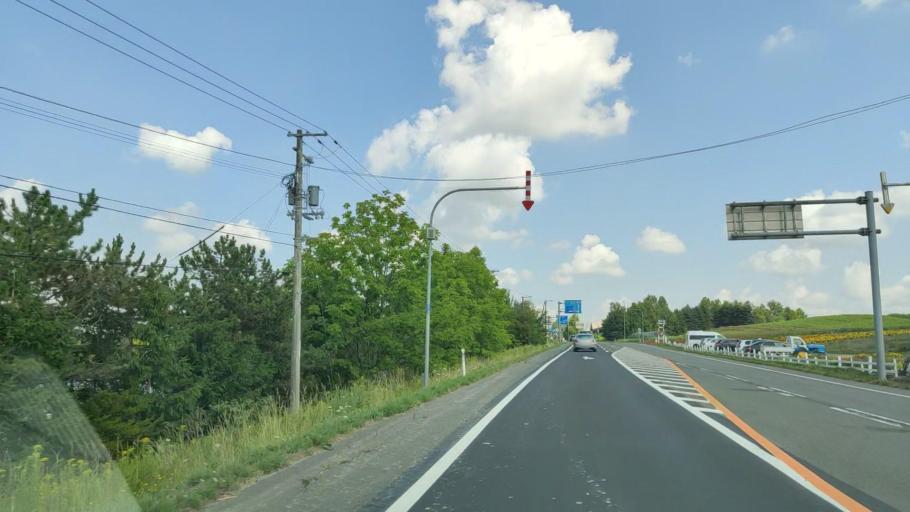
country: JP
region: Hokkaido
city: Shimo-furano
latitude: 43.5418
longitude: 142.4386
